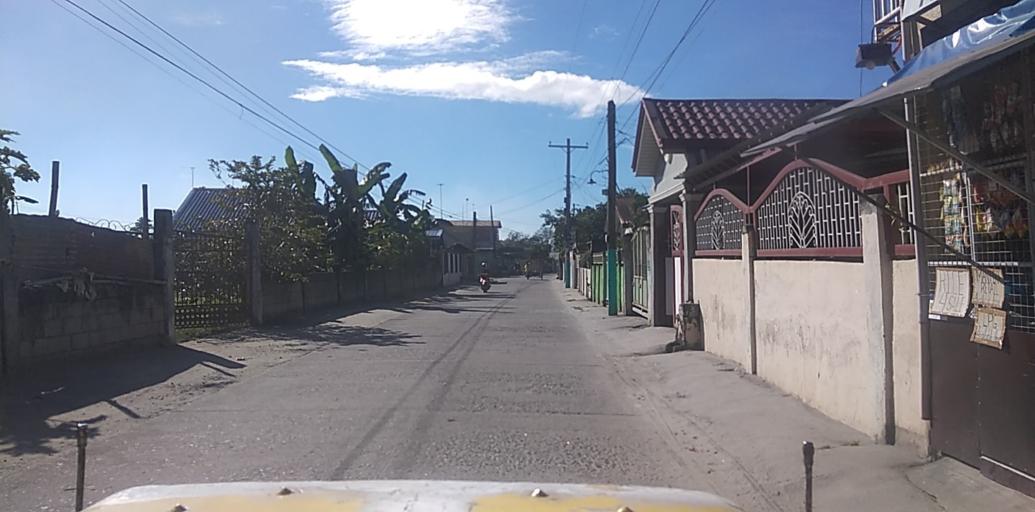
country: PH
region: Central Luzon
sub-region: Province of Pampanga
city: San Patricio
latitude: 15.1039
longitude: 120.7137
